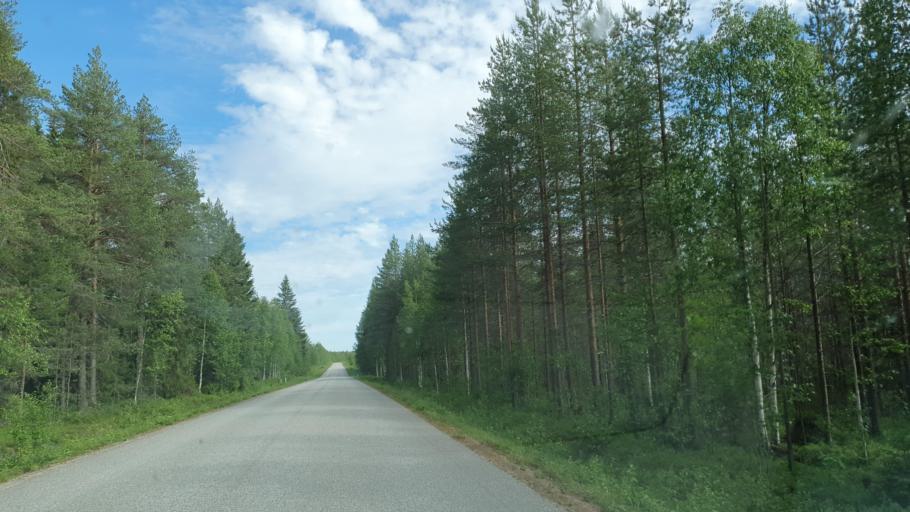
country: FI
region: Kainuu
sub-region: Kehys-Kainuu
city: Suomussalmi
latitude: 64.5509
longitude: 29.2269
